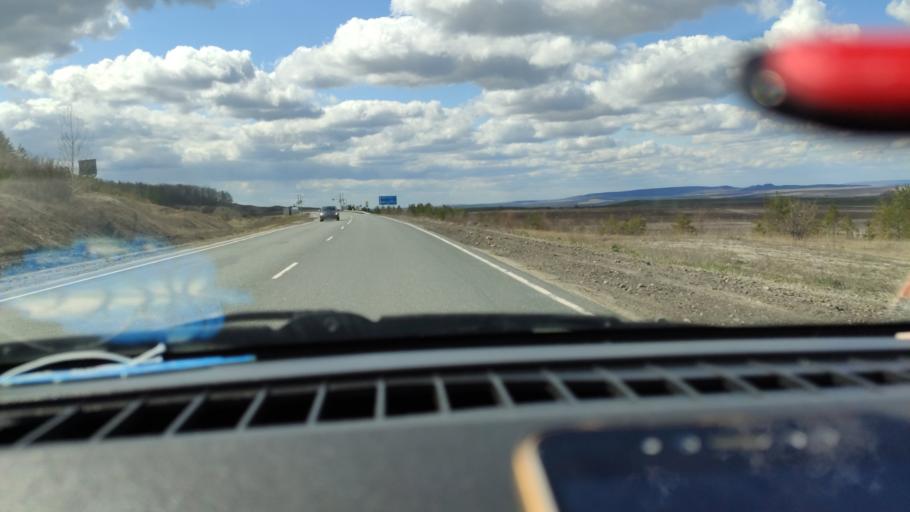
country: RU
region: Saratov
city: Alekseyevka
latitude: 52.3887
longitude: 47.9754
